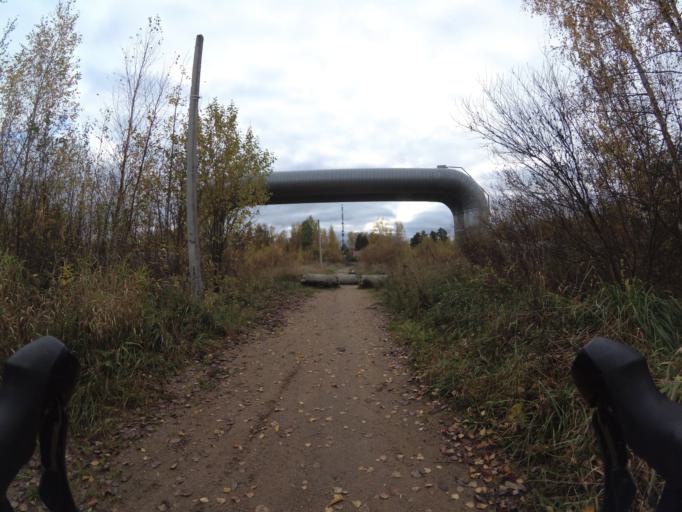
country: RU
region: St.-Petersburg
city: Lakhtinskiy
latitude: 60.0052
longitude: 30.1438
